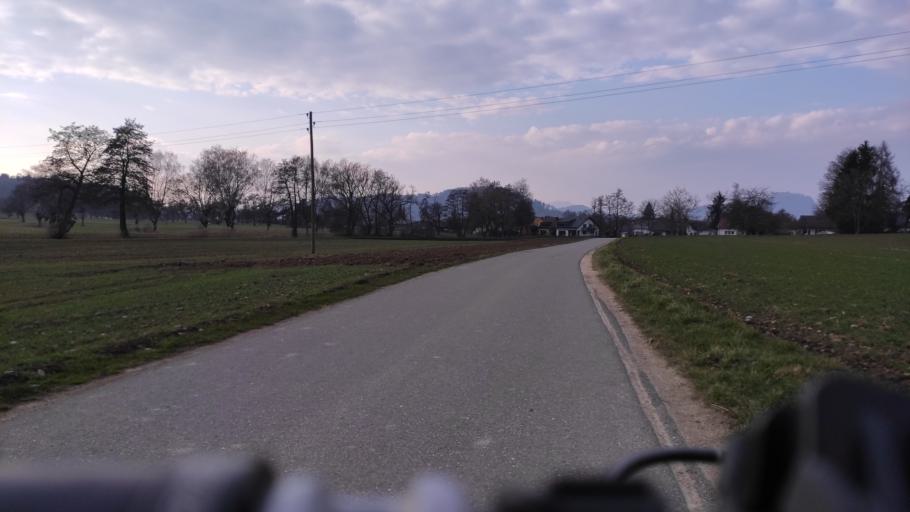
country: DE
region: Baden-Wuerttemberg
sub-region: Freiburg Region
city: Rielasingen-Worblingen
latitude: 47.7195
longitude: 8.8511
